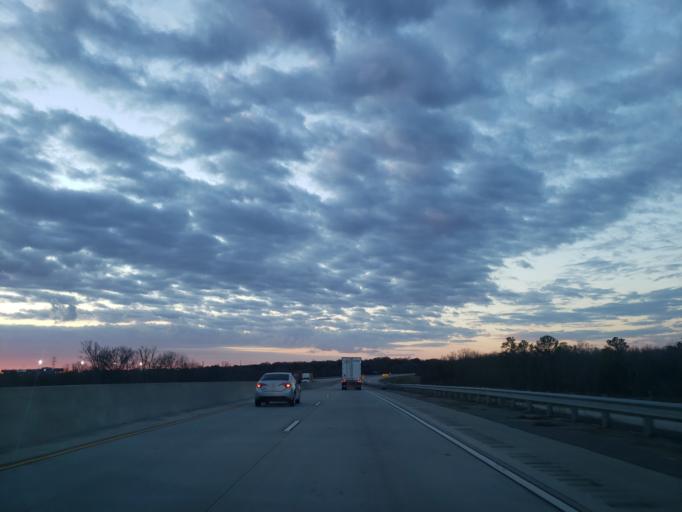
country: US
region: Georgia
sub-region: Chatham County
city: Port Wentworth
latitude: 32.1362
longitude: -81.1660
